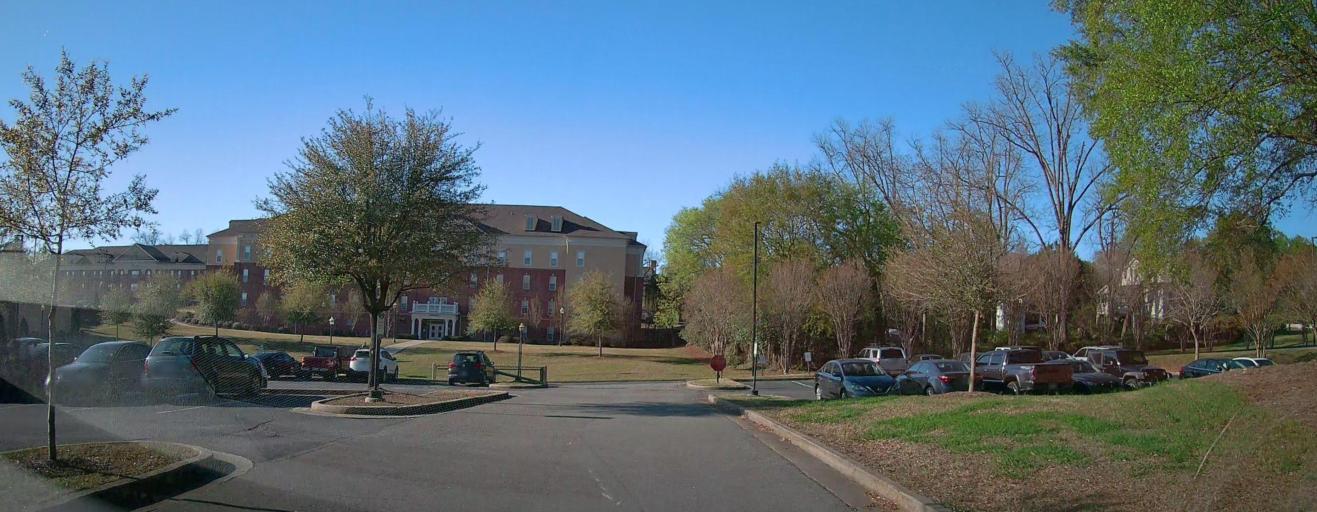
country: US
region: Georgia
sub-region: Baldwin County
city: Milledgeville
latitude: 33.0764
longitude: -83.2318
